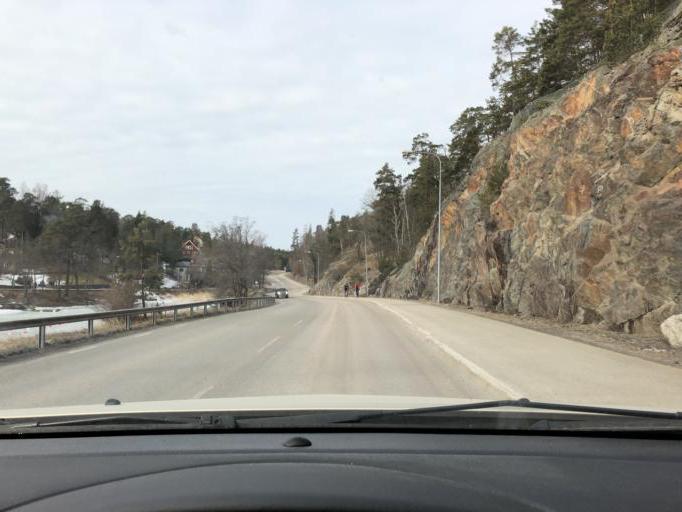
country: SE
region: Stockholm
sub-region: Nacka Kommun
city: Boo
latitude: 59.3343
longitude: 18.3018
